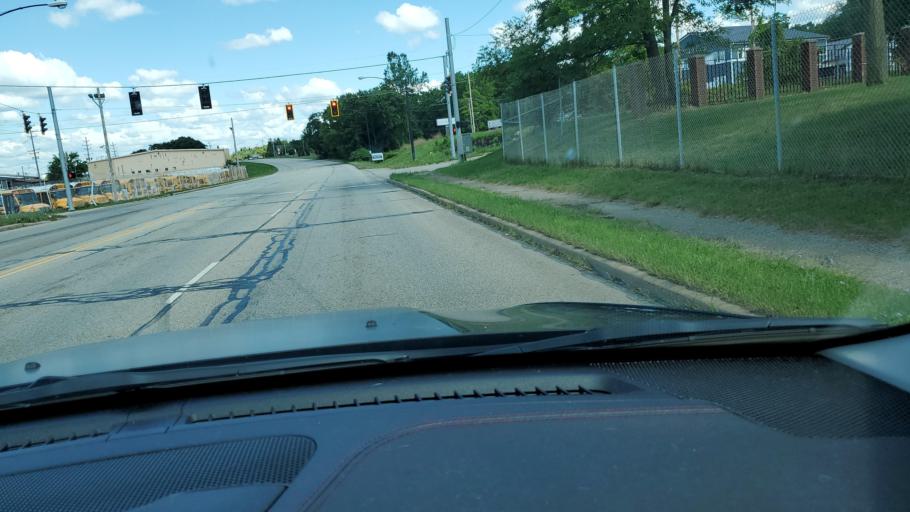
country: US
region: Ohio
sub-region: Mahoning County
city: Youngstown
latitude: 41.1137
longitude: -80.6676
